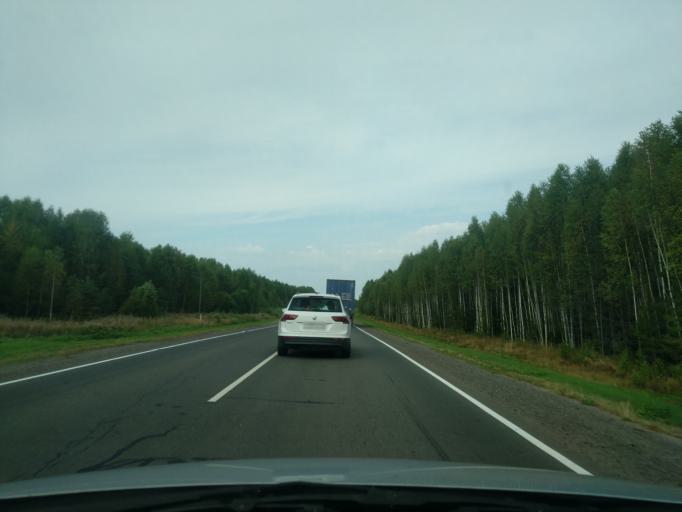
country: RU
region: Kirov
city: Leninskoye
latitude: 58.2844
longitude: 47.2614
